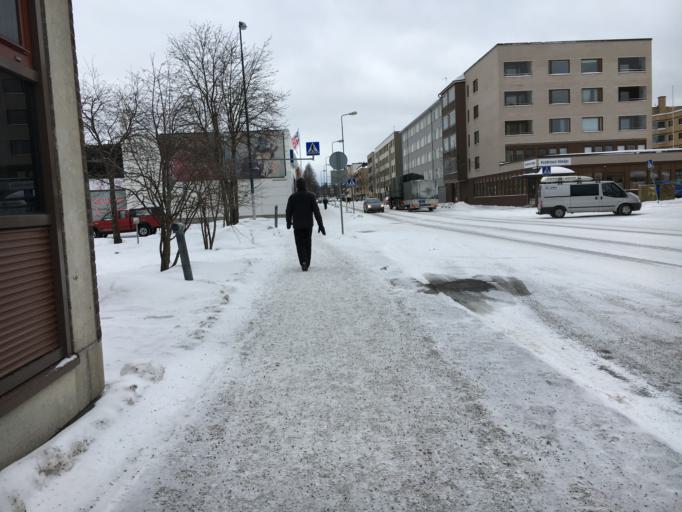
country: FI
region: Kainuu
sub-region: Kajaani
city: Kajaani
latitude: 64.2235
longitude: 27.7334
